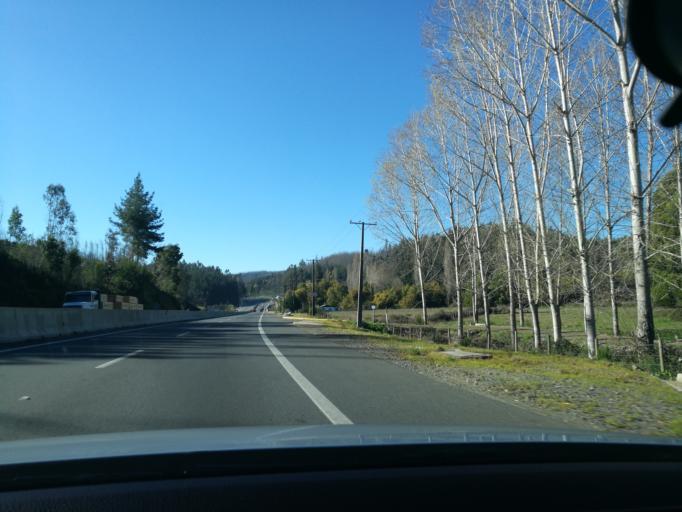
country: CL
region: Biobio
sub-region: Provincia de Concepcion
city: Penco
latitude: -36.8501
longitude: -72.9028
